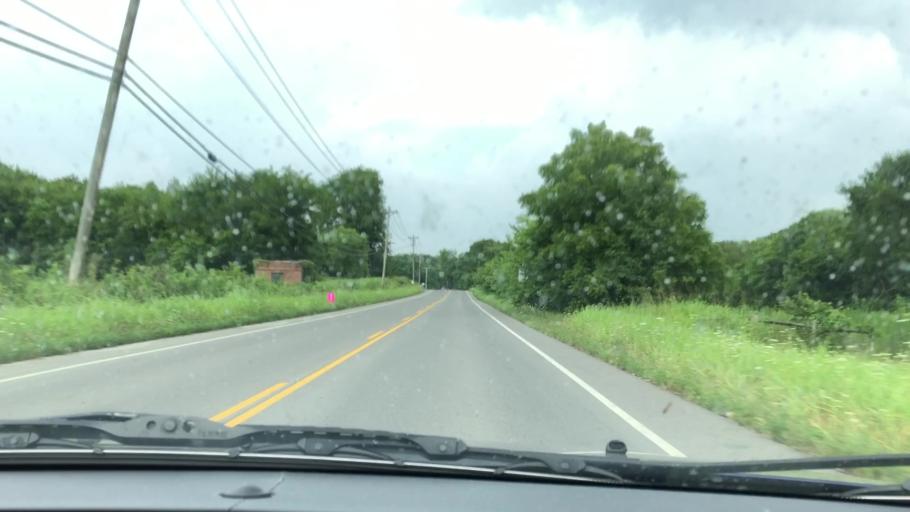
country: US
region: Tennessee
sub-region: Williamson County
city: Franklin
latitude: 35.8952
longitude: -86.9199
